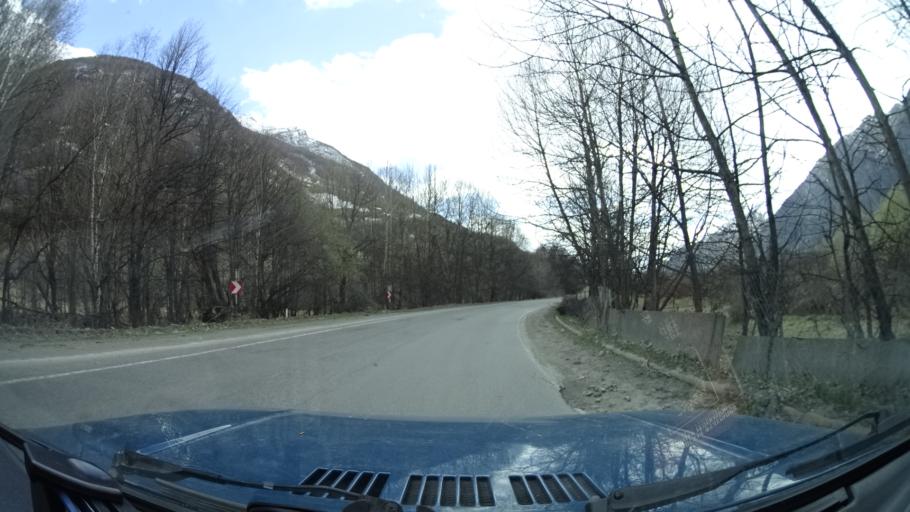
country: GE
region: Mtskheta-Mtianeti
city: Step'antsminda
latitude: 42.6448
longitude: 44.6408
